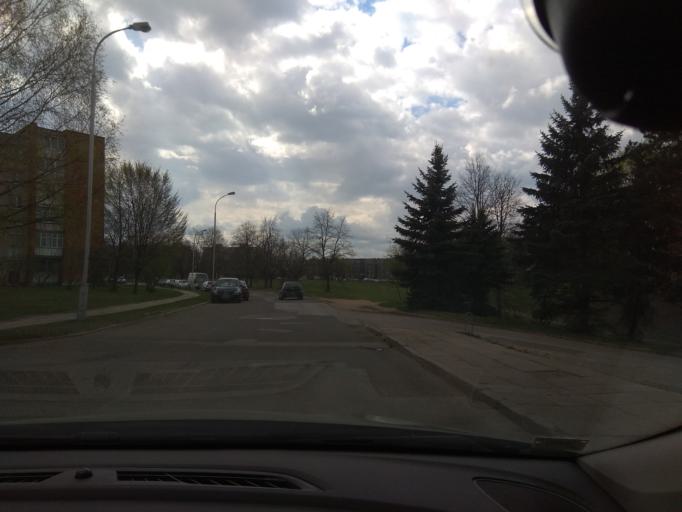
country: LT
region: Marijampoles apskritis
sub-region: Marijampole Municipality
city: Marijampole
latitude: 54.5711
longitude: 23.3609
